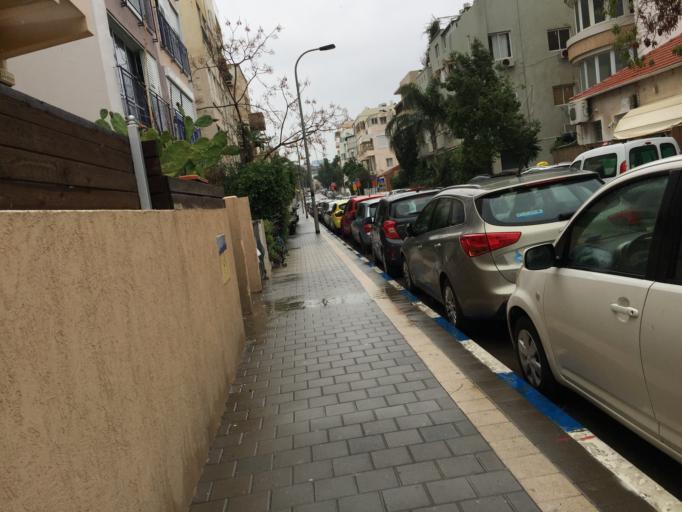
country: IL
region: Tel Aviv
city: Tel Aviv
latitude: 32.0715
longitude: 34.7658
